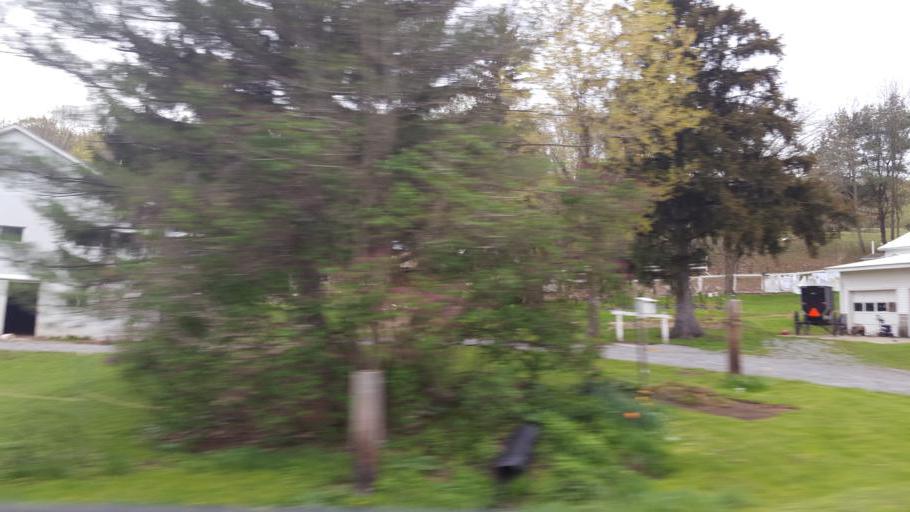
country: US
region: Pennsylvania
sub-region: Tioga County
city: Westfield
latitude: 42.0447
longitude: -77.4664
